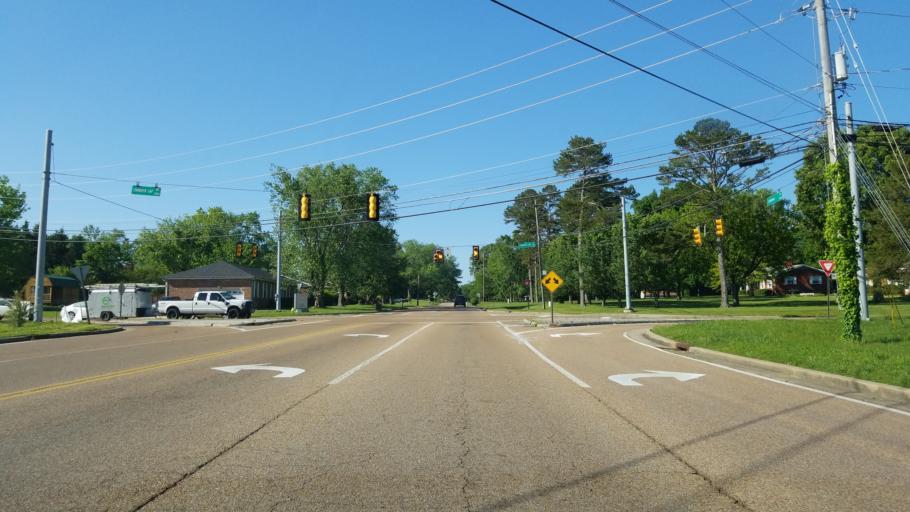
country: US
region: Tennessee
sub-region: Hamilton County
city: East Brainerd
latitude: 35.0449
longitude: -85.1281
